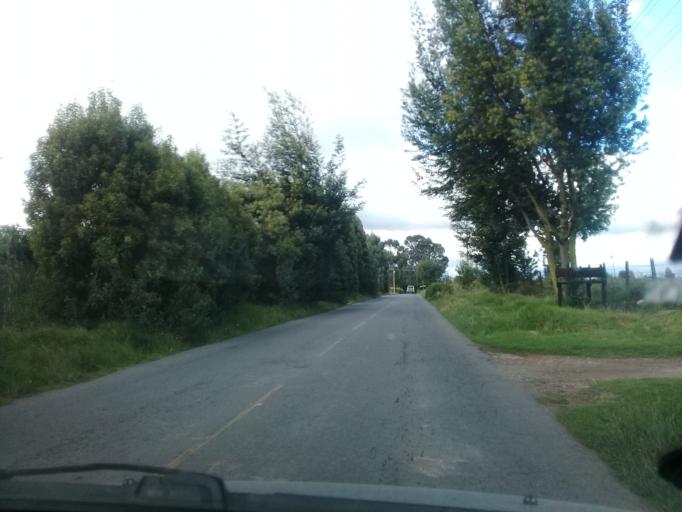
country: CO
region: Cundinamarca
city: Subachoque
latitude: 4.8977
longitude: -74.1941
